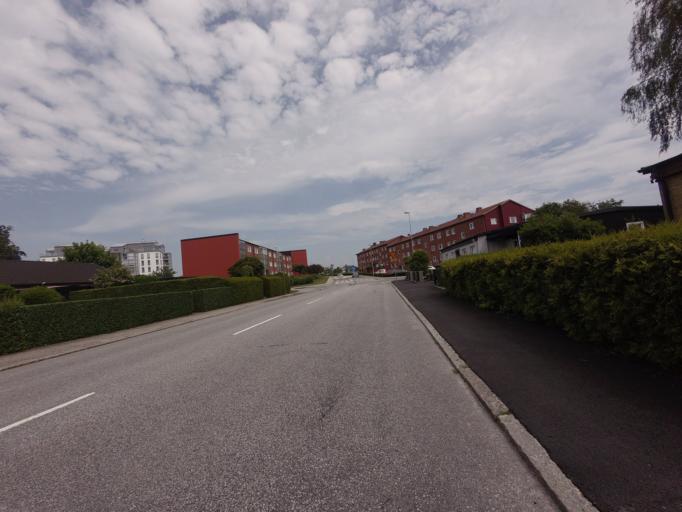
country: SE
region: Skane
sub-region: Ystads Kommun
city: Ystad
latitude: 55.4288
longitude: 13.8028
